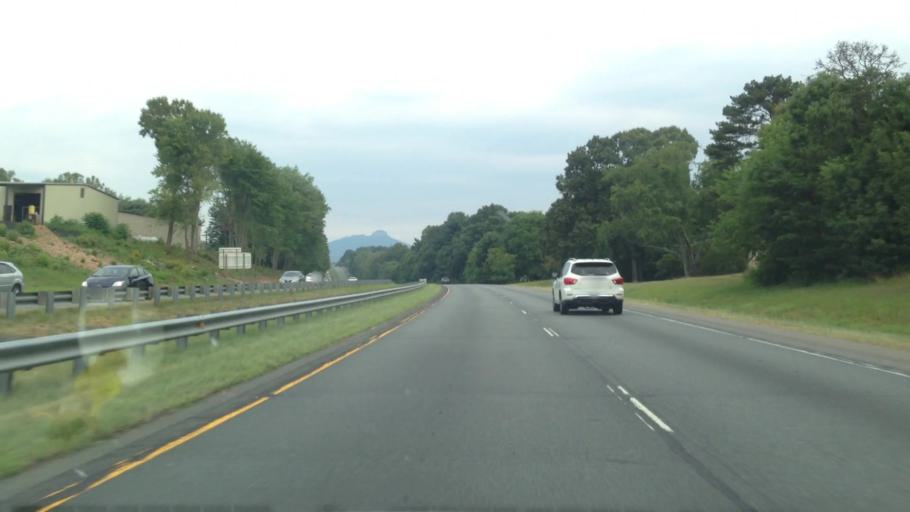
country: US
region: North Carolina
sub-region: Stokes County
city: King
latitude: 36.2752
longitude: -80.3797
